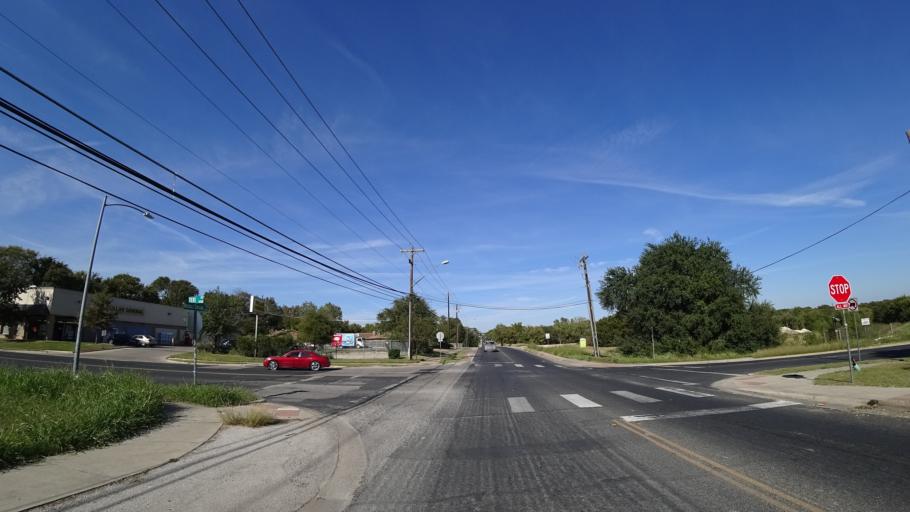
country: US
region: Texas
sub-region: Travis County
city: Austin
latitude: 30.1948
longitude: -97.7379
